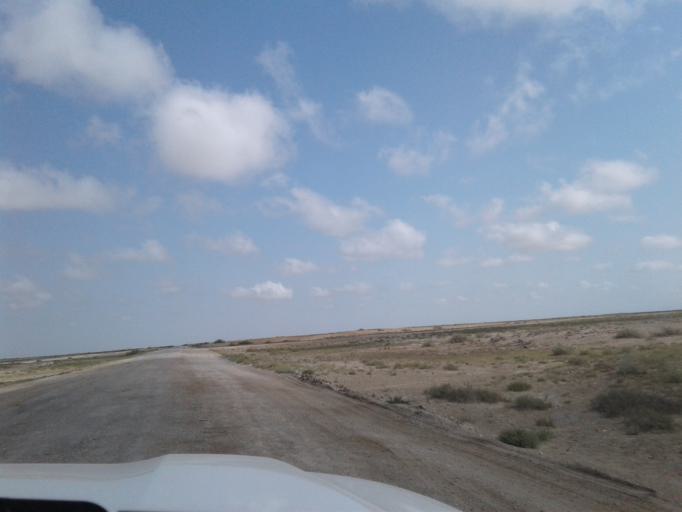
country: IR
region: Golestan
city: Gomishan
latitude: 37.6232
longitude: 53.9277
